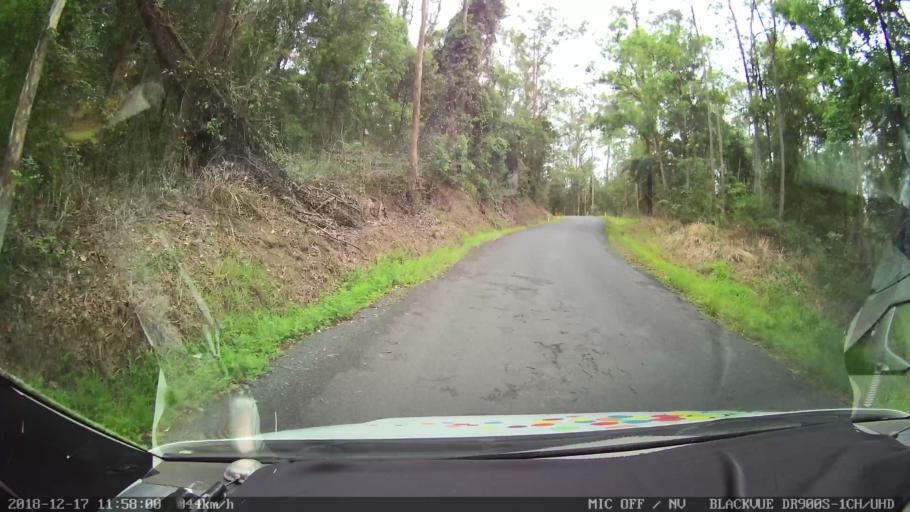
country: AU
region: New South Wales
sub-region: Kyogle
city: Kyogle
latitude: -28.5380
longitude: 152.5710
